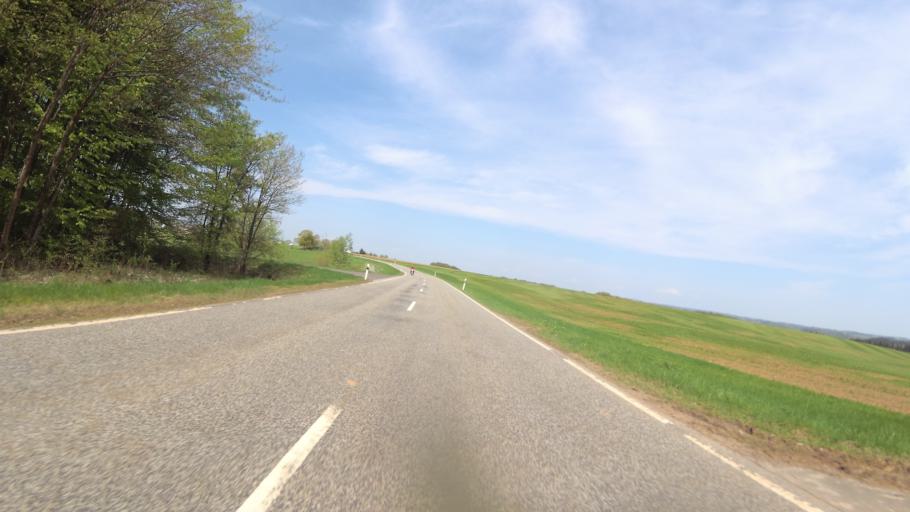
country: DE
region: Rheinland-Pfalz
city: Hontheim
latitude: 50.0458
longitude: 6.9926
